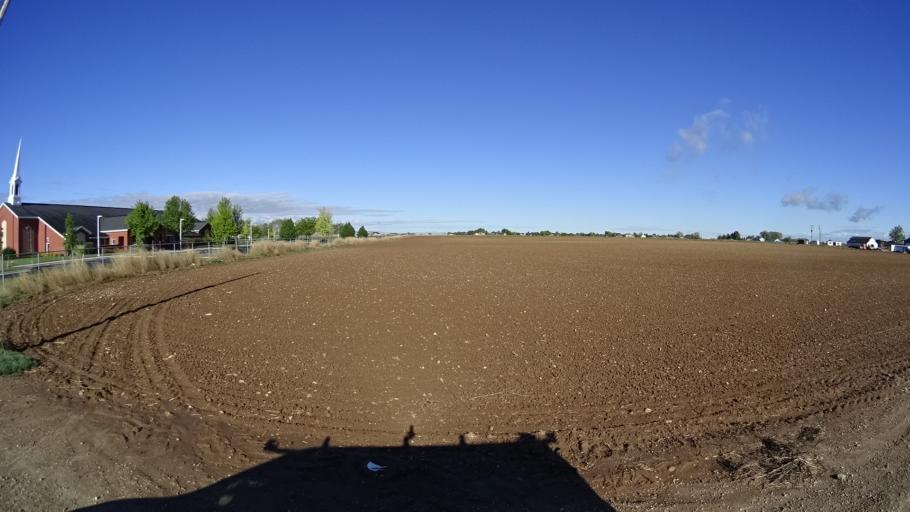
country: US
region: Idaho
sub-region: Ada County
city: Kuna
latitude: 43.5267
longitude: -116.4136
